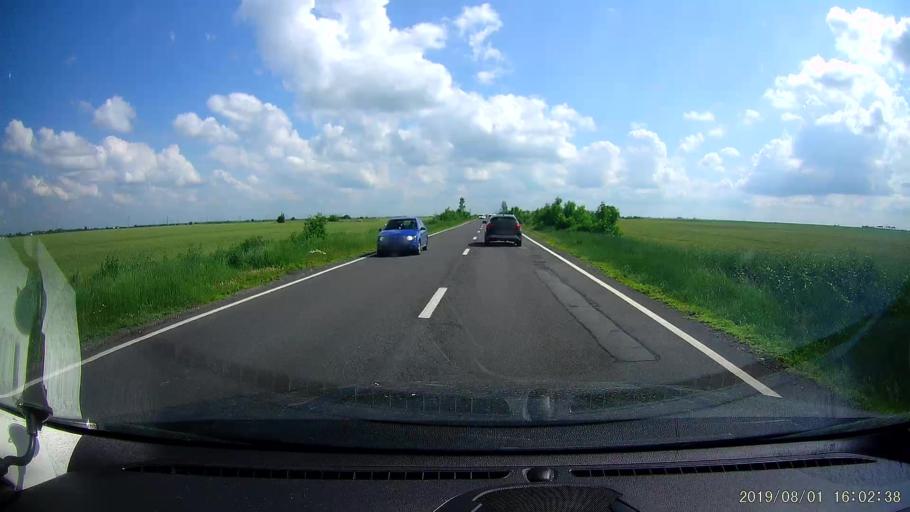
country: RO
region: Ialomita
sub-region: Comuna Ciulnita
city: Ciulnita
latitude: 44.4861
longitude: 27.3867
